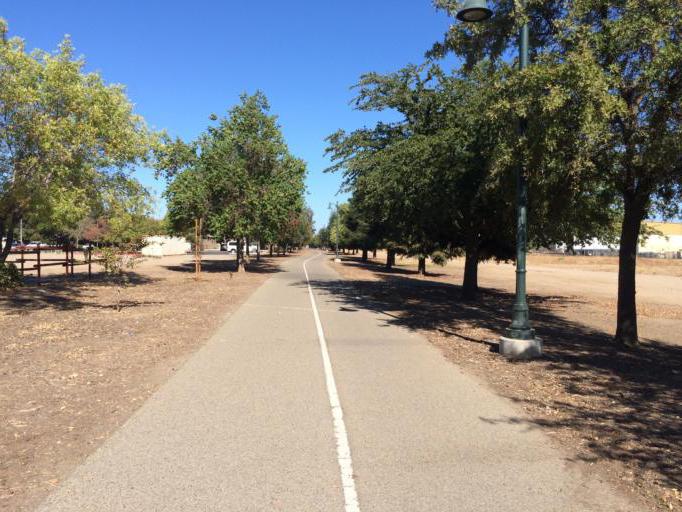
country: US
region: California
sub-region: Fresno County
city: Clovis
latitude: 36.8270
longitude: -119.7000
